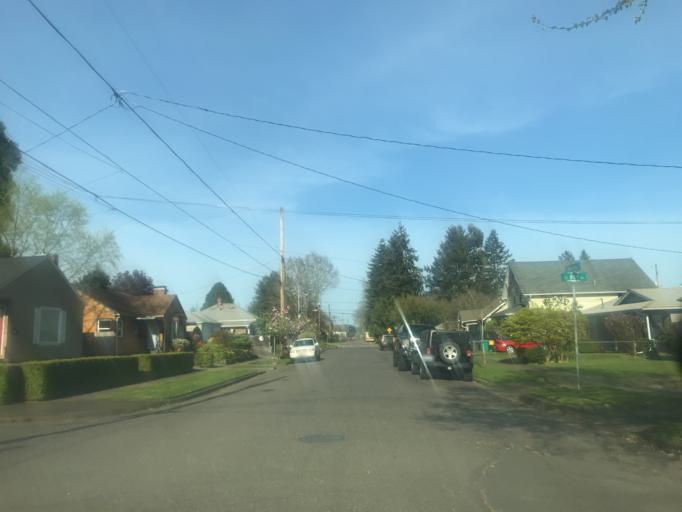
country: US
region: Oregon
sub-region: Multnomah County
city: Lents
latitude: 45.5015
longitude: -122.5806
